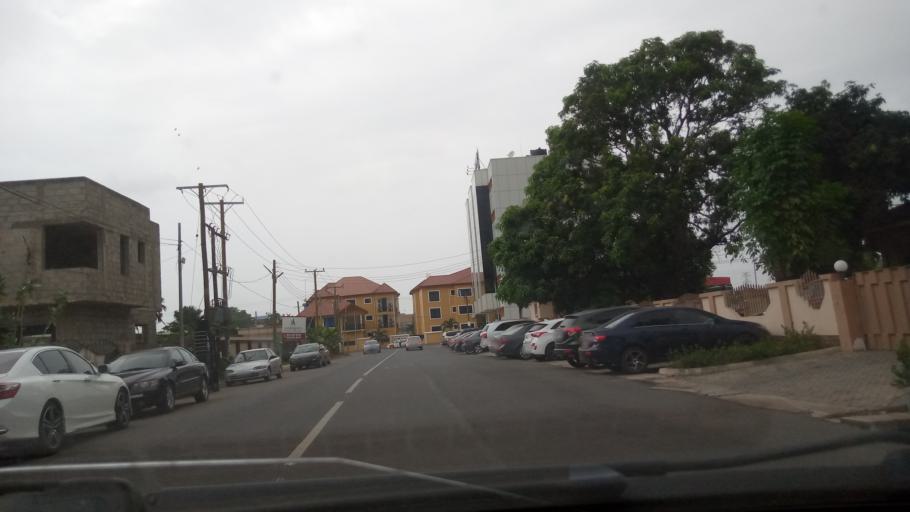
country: GH
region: Greater Accra
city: Dome
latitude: 5.6149
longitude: -0.1931
